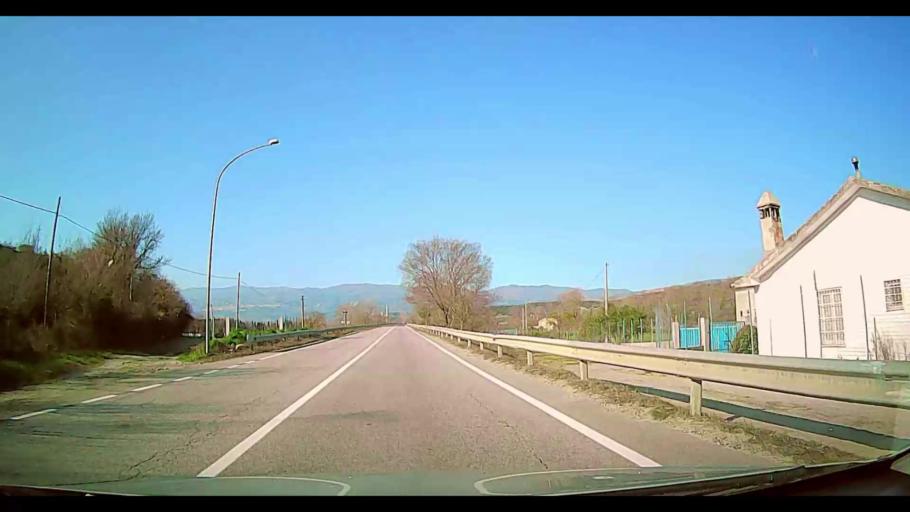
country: IT
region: Calabria
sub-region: Provincia di Crotone
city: Belvedere Spinello
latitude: 39.1881
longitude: 16.8608
